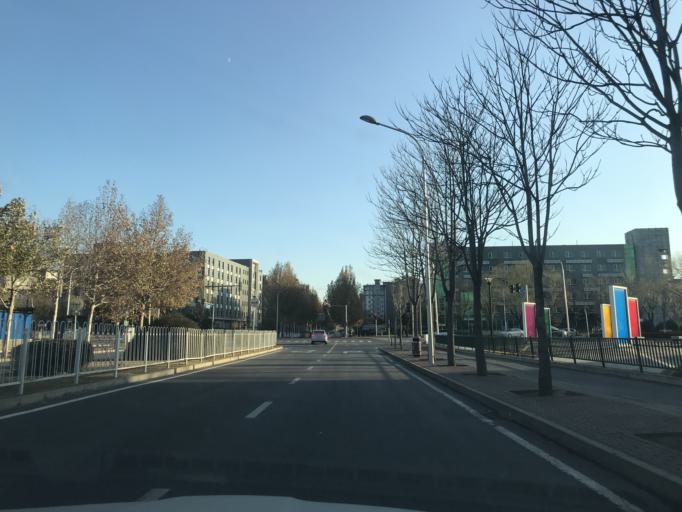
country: CN
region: Beijing
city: Xibeiwang
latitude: 40.0686
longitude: 116.2472
